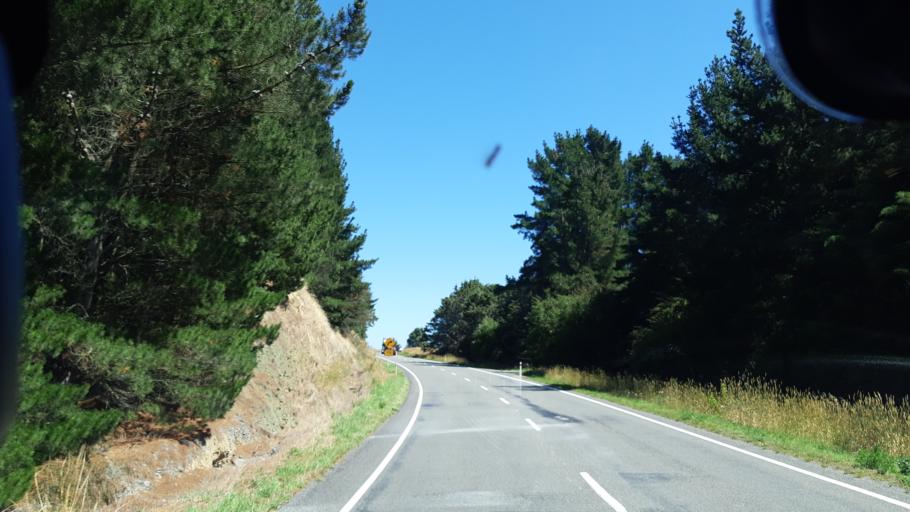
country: NZ
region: Canterbury
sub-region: Kaikoura District
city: Kaikoura
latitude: -42.7515
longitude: 173.2719
